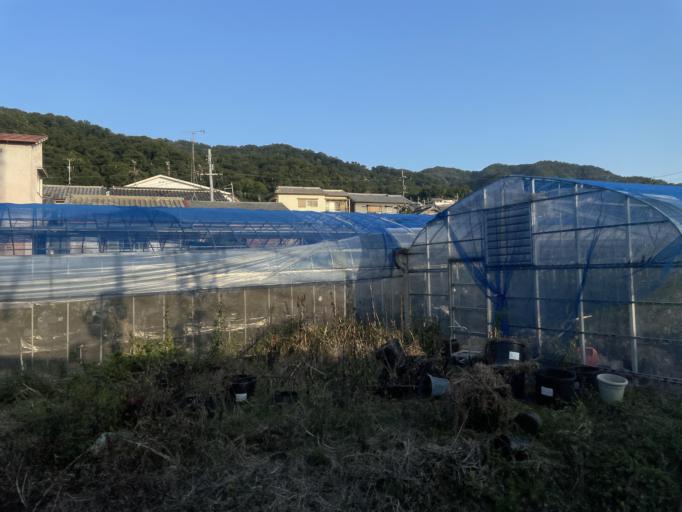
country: JP
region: Osaka
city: Daitocho
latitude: 34.6646
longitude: 135.6465
